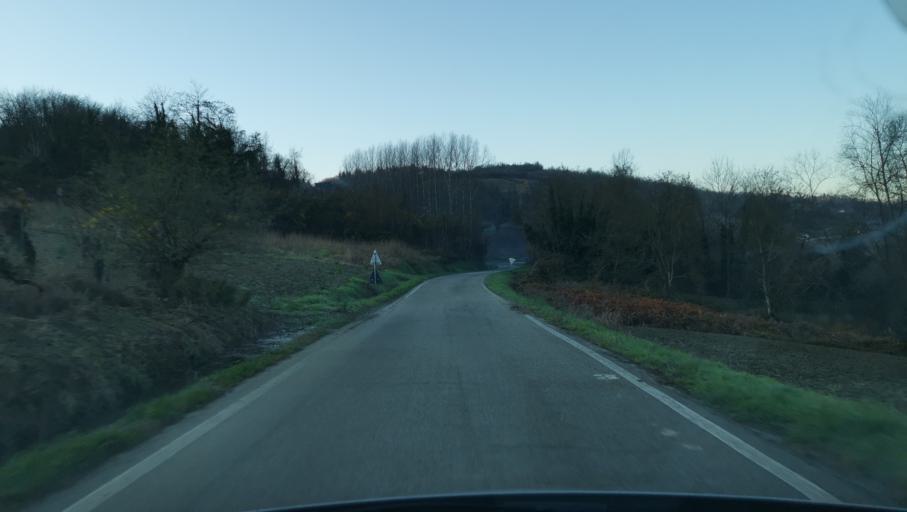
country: IT
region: Piedmont
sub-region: Provincia di Asti
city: Moncucco Torinese
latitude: 45.0677
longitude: 7.9419
